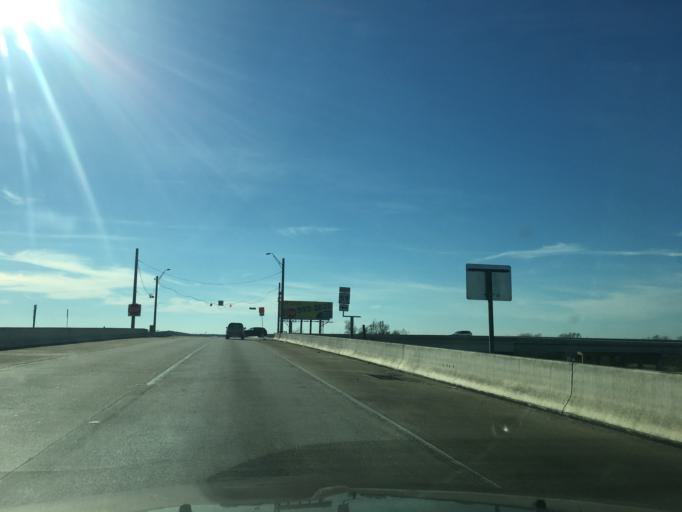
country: US
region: Texas
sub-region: Fort Bend County
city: Rosenberg
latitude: 29.5247
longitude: -95.8738
